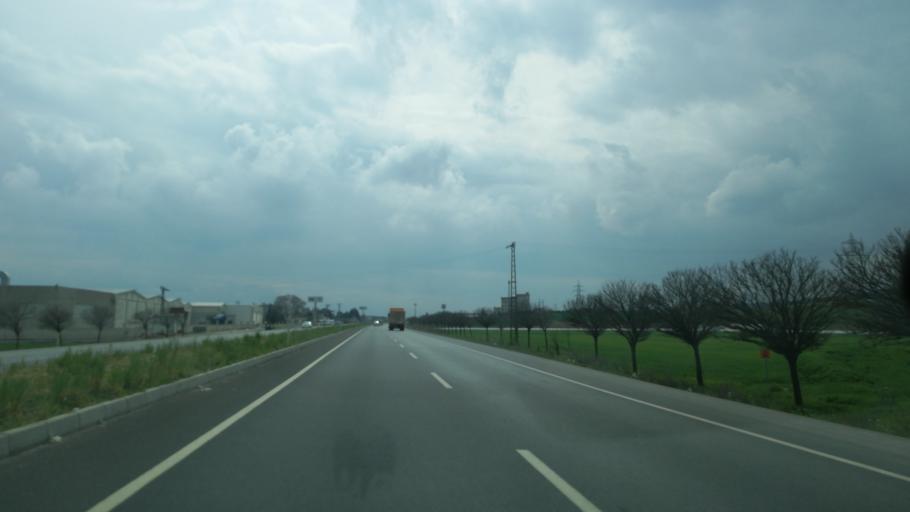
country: TR
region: Kahramanmaras
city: Turkoglu
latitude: 37.4458
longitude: 36.8876
